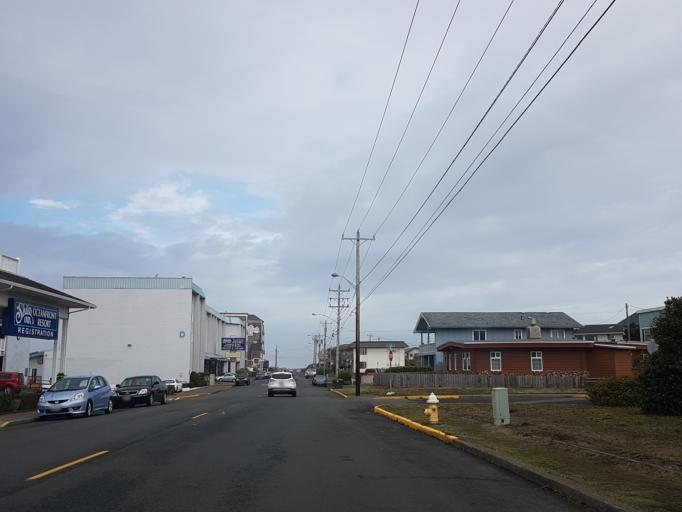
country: US
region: Oregon
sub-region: Lincoln County
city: Newport
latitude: 44.6321
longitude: -124.0633
